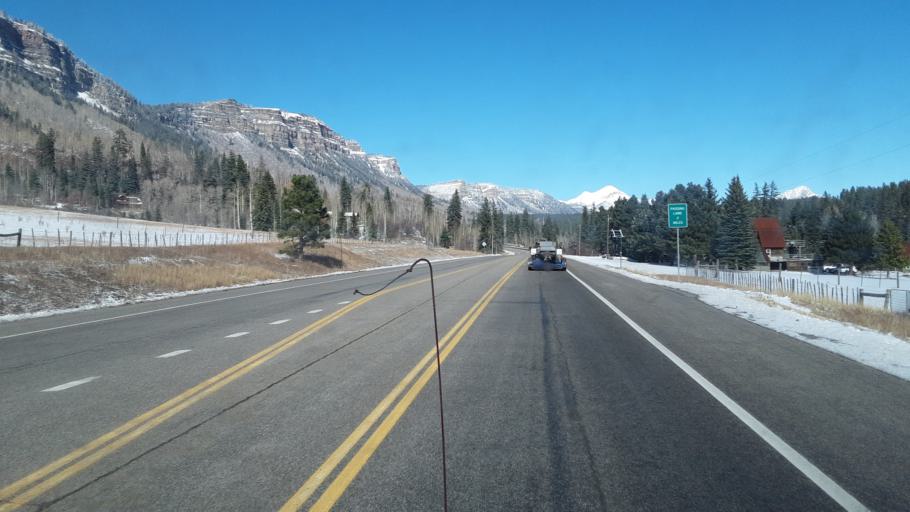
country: US
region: Colorado
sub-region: La Plata County
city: Durango
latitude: 37.5309
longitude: -107.8183
